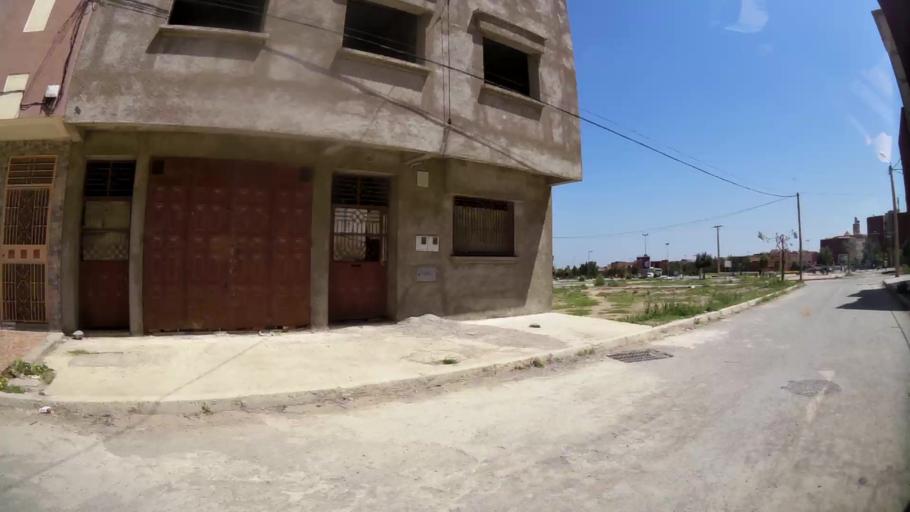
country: MA
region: Oriental
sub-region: Oujda-Angad
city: Oujda
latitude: 34.6822
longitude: -1.9476
